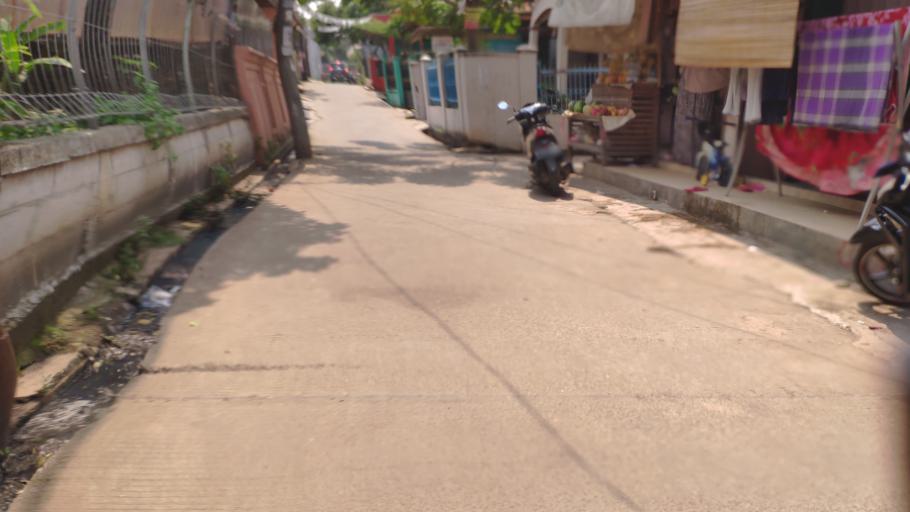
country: ID
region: West Java
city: Pamulang
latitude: -6.3416
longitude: 106.7936
